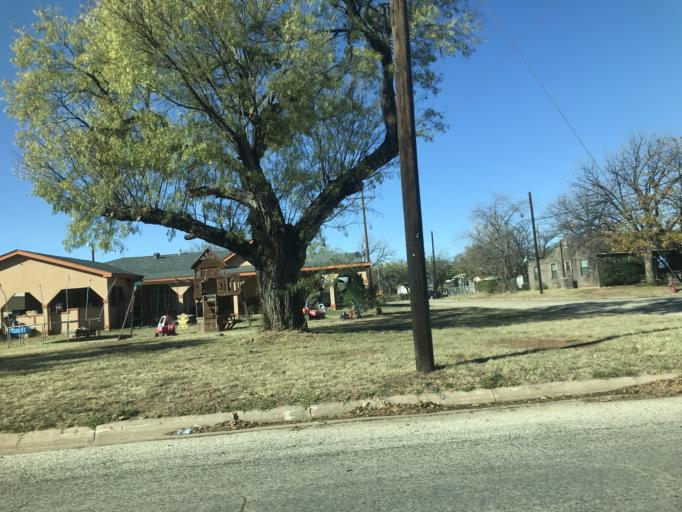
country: US
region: Texas
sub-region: Taylor County
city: Abilene
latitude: 32.4577
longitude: -99.7488
